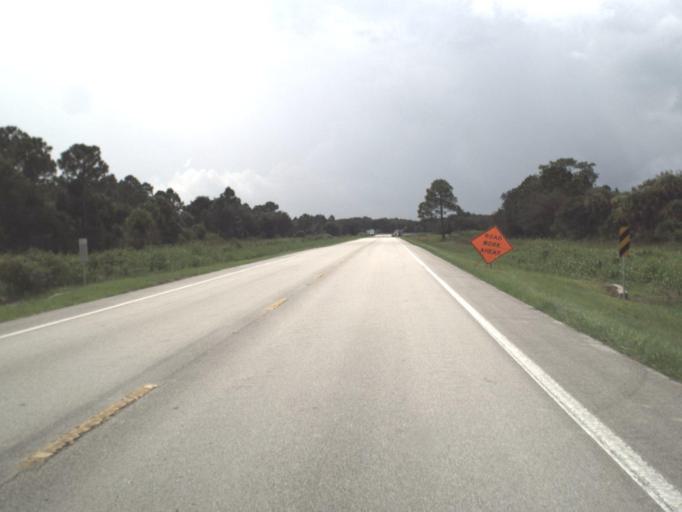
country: US
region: Florida
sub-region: Sarasota County
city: Warm Mineral Springs
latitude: 27.1937
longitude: -82.1915
